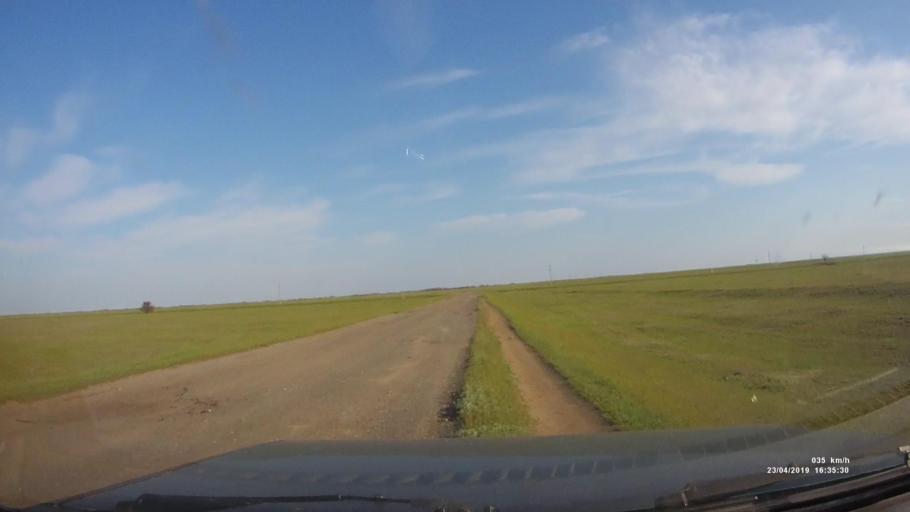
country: RU
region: Kalmykiya
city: Priyutnoye
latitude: 46.3305
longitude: 43.1376
